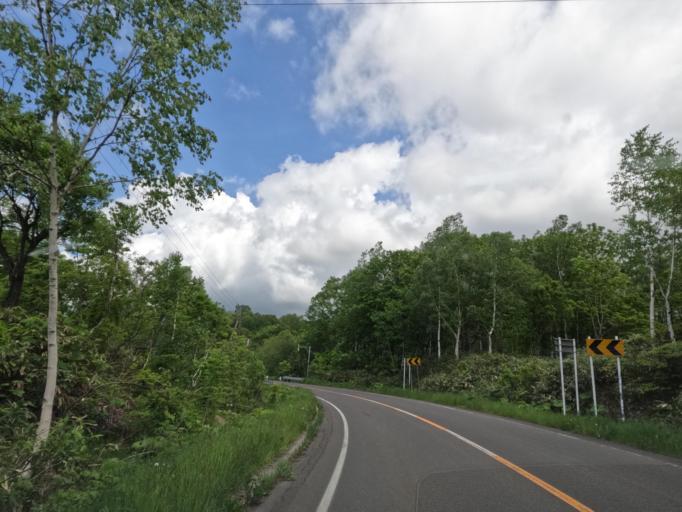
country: JP
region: Hokkaido
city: Tobetsu
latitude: 43.4955
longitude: 141.6092
